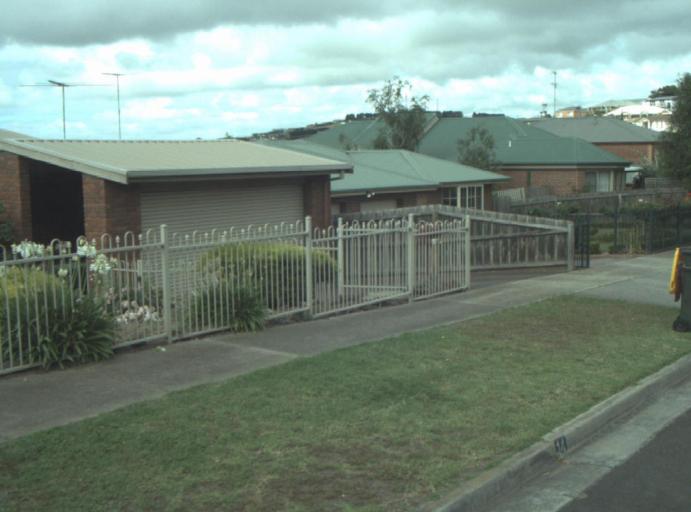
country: AU
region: Victoria
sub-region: Greater Geelong
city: Wandana Heights
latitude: -38.1644
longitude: 144.3122
